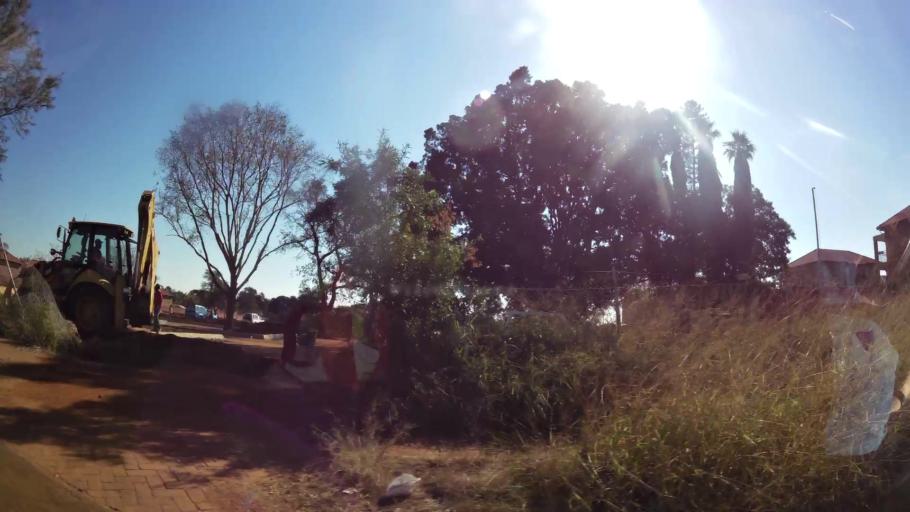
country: ZA
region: Gauteng
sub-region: City of Tshwane Metropolitan Municipality
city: Pretoria
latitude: -25.6747
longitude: 28.2396
